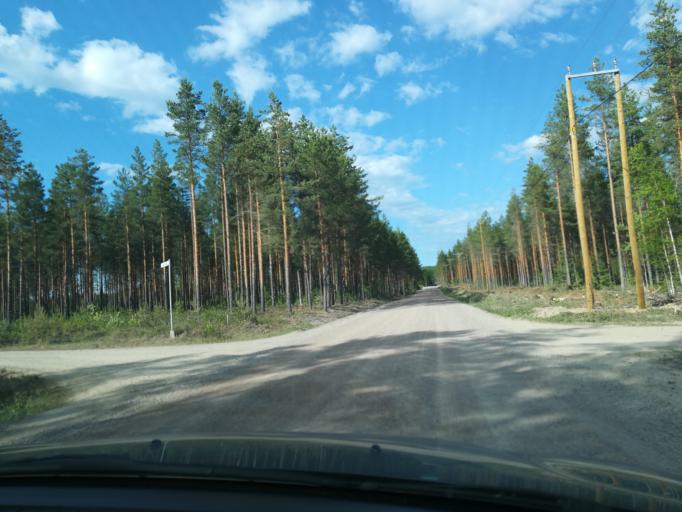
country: FI
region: Southern Savonia
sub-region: Savonlinna
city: Savonlinna
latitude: 61.6355
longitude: 28.7304
